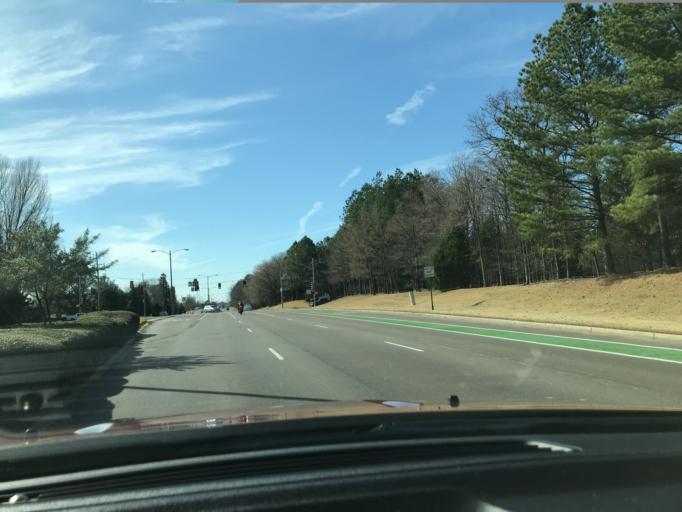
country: US
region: Tennessee
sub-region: Shelby County
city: Germantown
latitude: 35.0482
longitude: -89.7889
